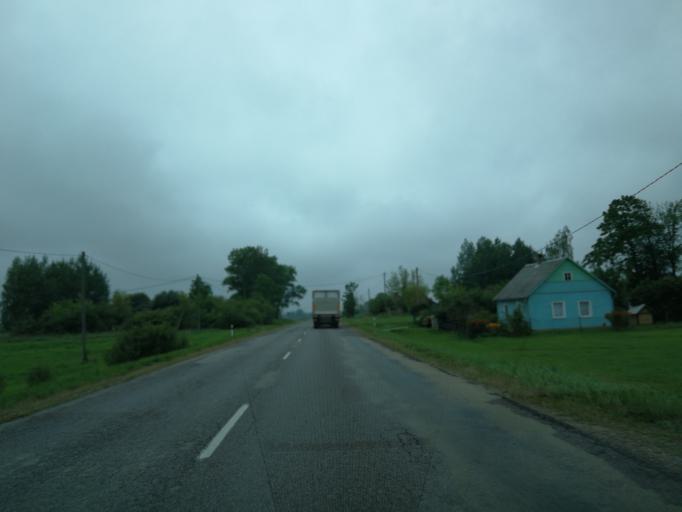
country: LV
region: Livani
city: Livani
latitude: 56.3469
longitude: 26.2900
